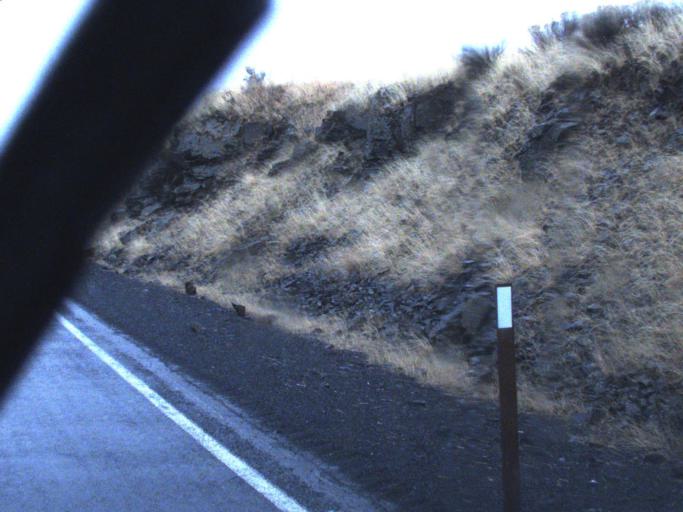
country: US
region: Washington
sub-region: Spokane County
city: Medical Lake
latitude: 47.2571
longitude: -117.9310
